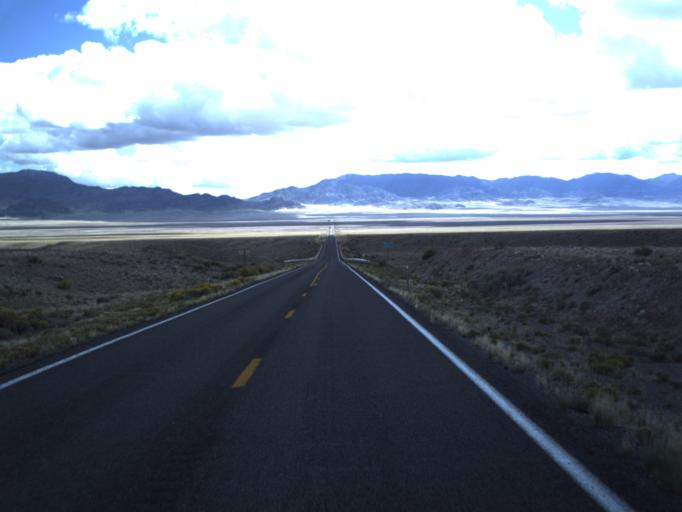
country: US
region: Utah
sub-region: Beaver County
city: Milford
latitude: 38.5693
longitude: -113.7820
